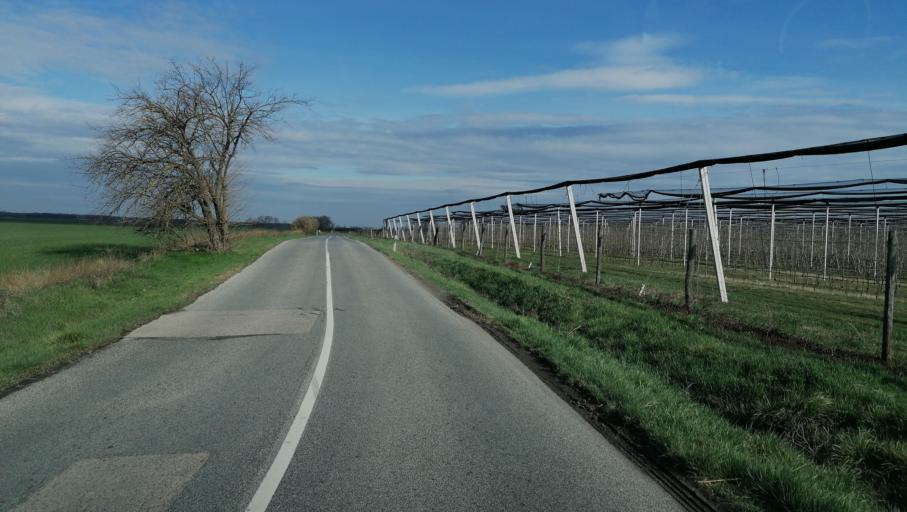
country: HU
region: Pest
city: Rackeve
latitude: 47.1097
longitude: 18.9406
